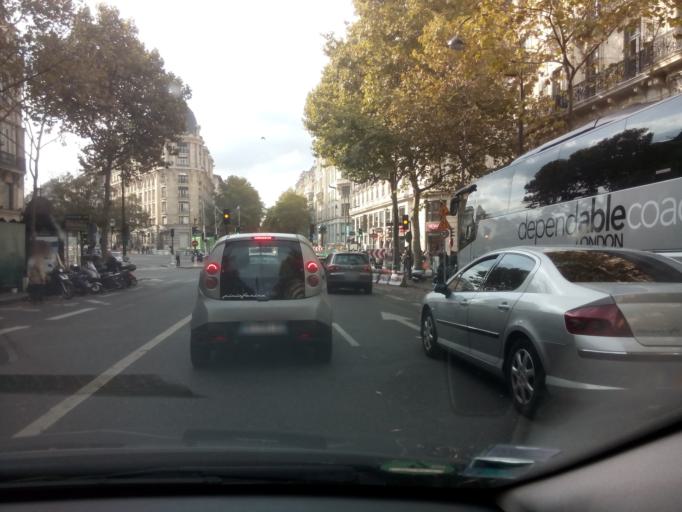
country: FR
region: Ile-de-France
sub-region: Paris
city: Paris
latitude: 48.8720
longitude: 2.3409
